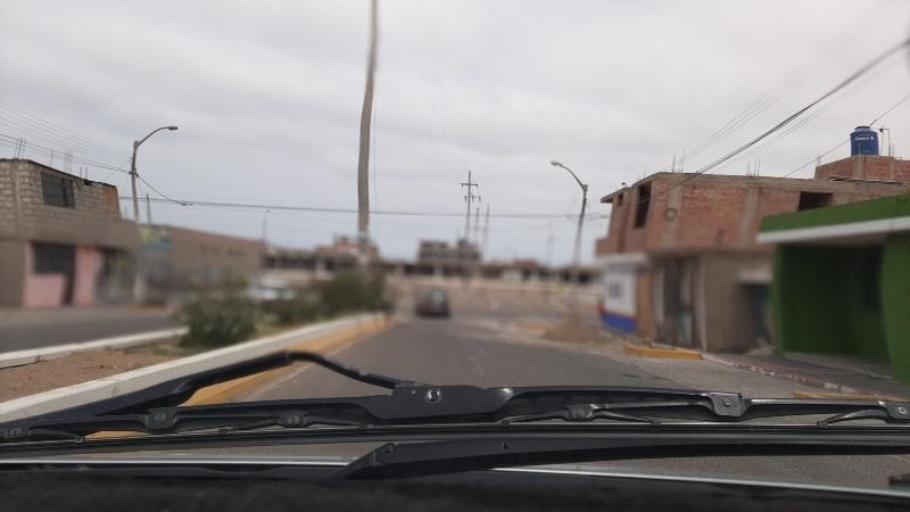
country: PE
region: Moquegua
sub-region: Provincia de Ilo
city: Ilo
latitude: -17.6474
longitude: -71.3270
